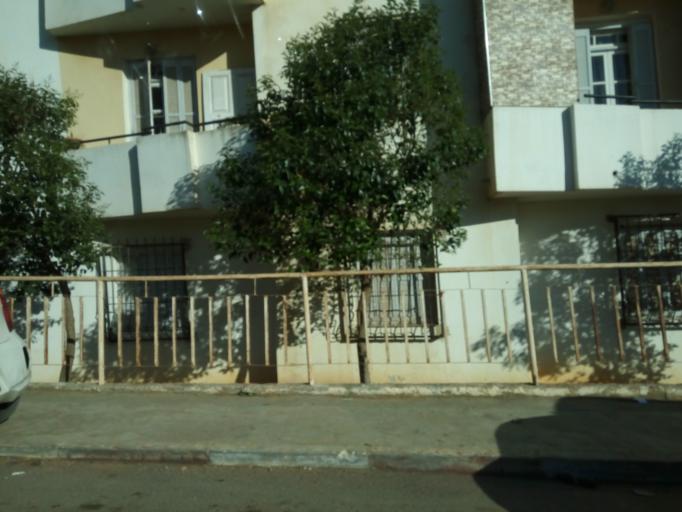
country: DZ
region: Tipaza
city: Saoula
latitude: 36.7145
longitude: 3.0140
